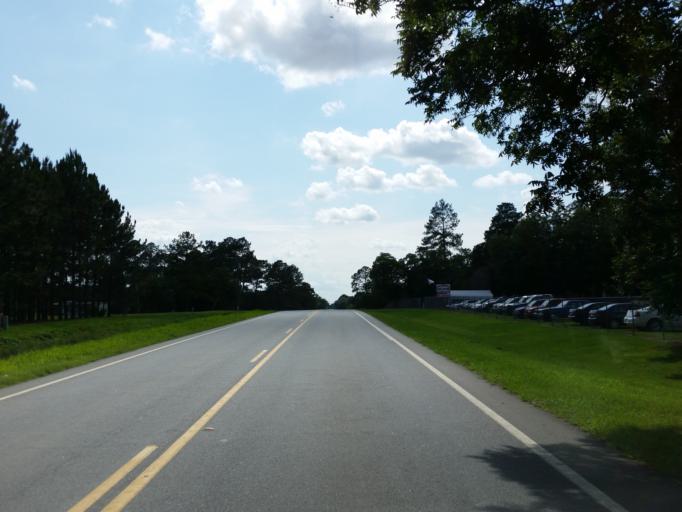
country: US
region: Georgia
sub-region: Turner County
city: Ashburn
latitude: 31.6589
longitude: -83.5777
